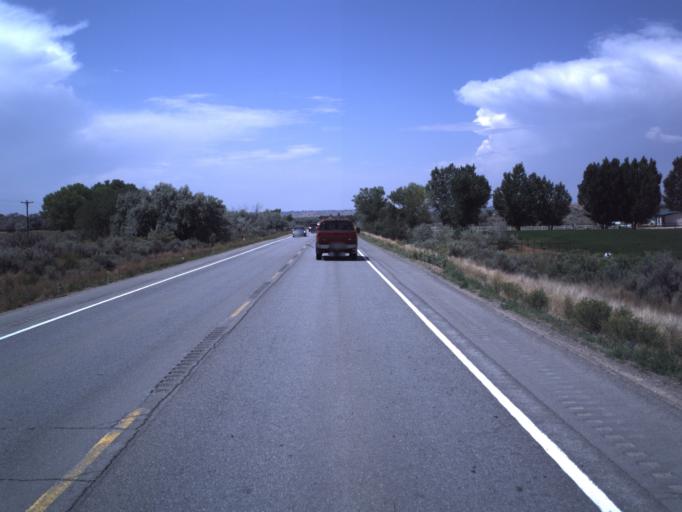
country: US
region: Utah
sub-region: Duchesne County
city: Roosevelt
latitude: 40.3032
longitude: -109.7853
